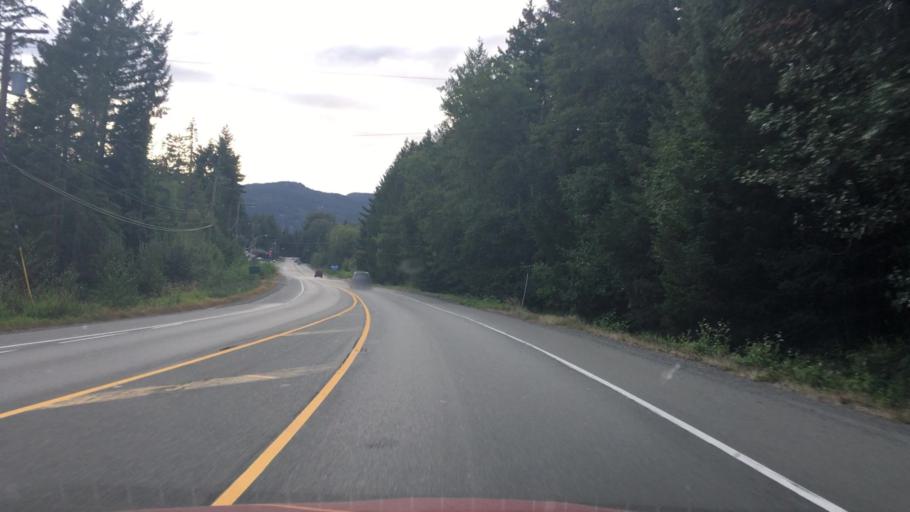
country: CA
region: British Columbia
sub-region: Regional District of Nanaimo
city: Parksville
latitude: 49.3125
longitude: -124.5114
